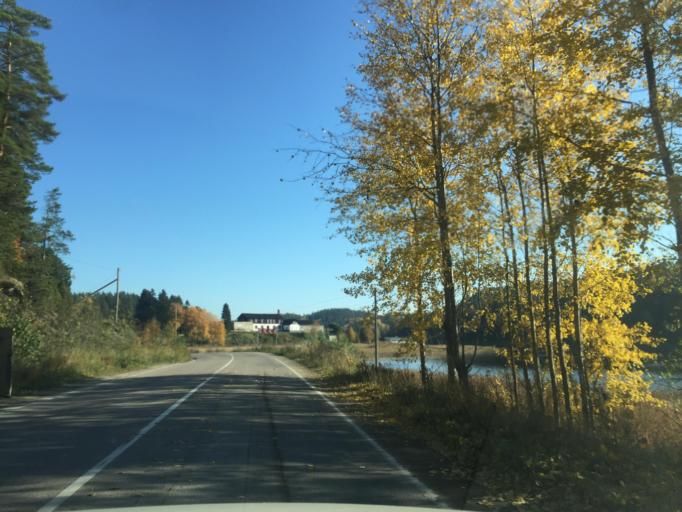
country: RU
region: Leningrad
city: Kuznechnoye
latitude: 61.2985
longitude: 29.9027
